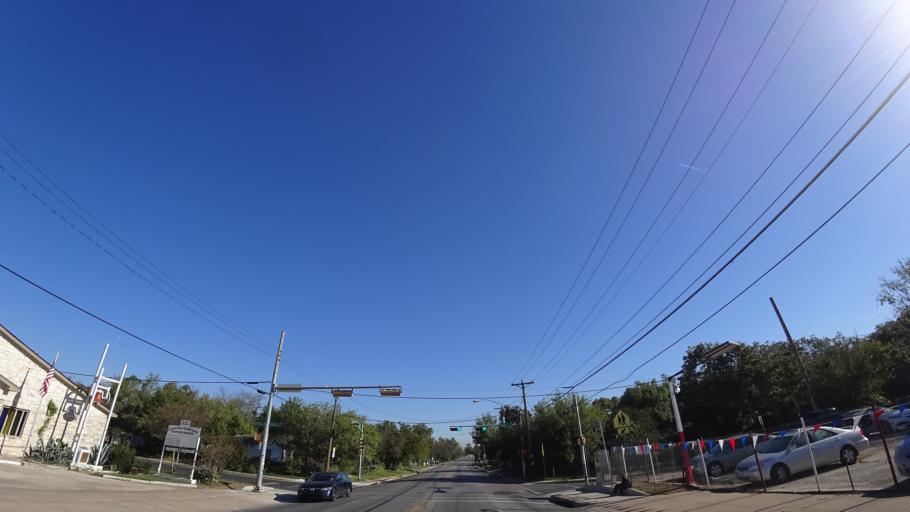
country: US
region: Texas
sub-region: Travis County
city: Austin
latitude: 30.2373
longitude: -97.6955
